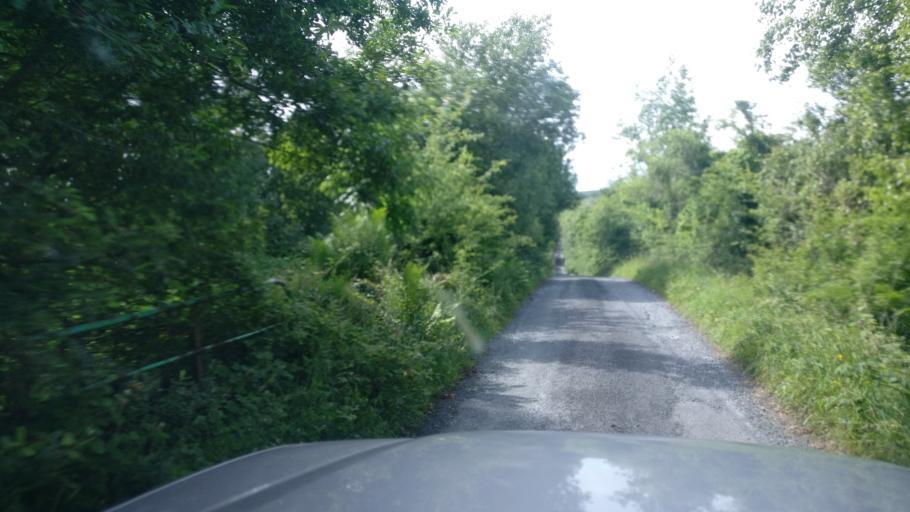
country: IE
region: Connaught
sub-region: County Galway
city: Gort
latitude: 53.0988
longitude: -8.6987
